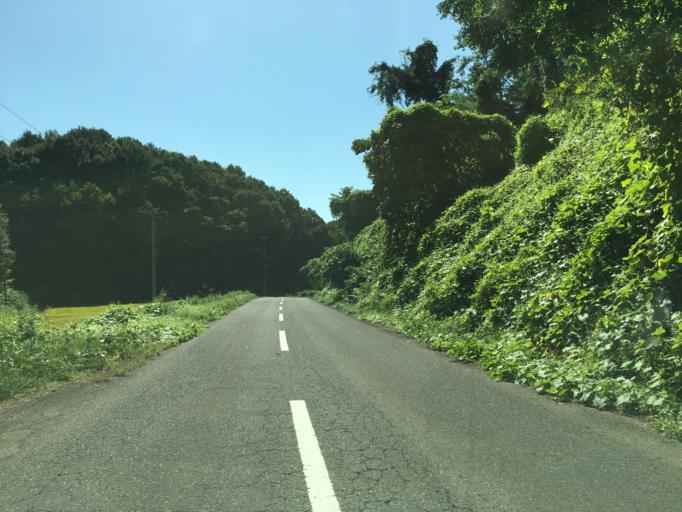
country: JP
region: Fukushima
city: Sukagawa
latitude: 37.2803
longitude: 140.4723
